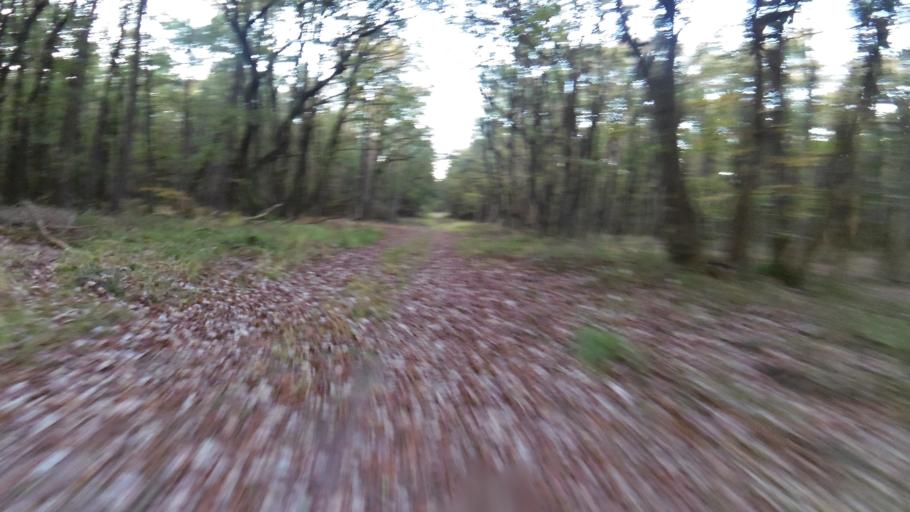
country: NL
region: Gelderland
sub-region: Gemeente Apeldoorn
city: Uddel
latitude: 52.2951
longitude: 5.8384
